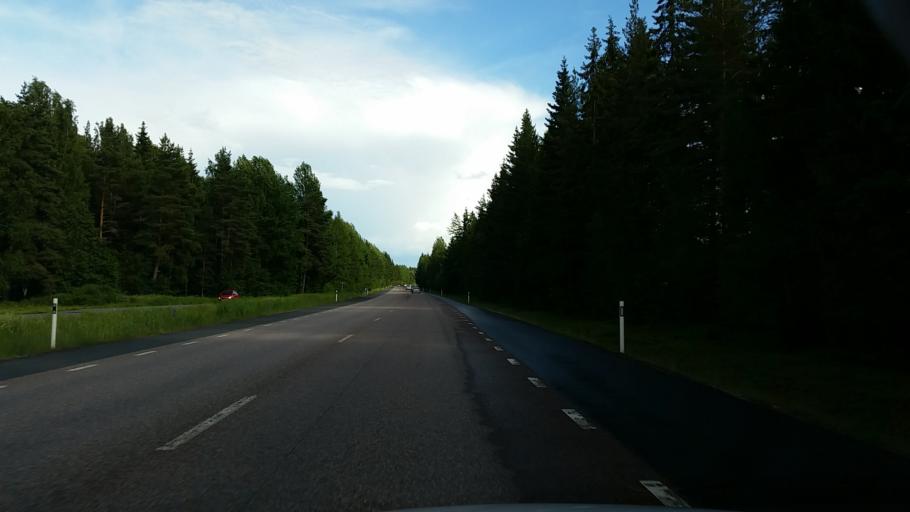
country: SE
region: Vaestmanland
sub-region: Fagersta Kommun
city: Fagersta
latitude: 60.0267
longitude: 15.6083
